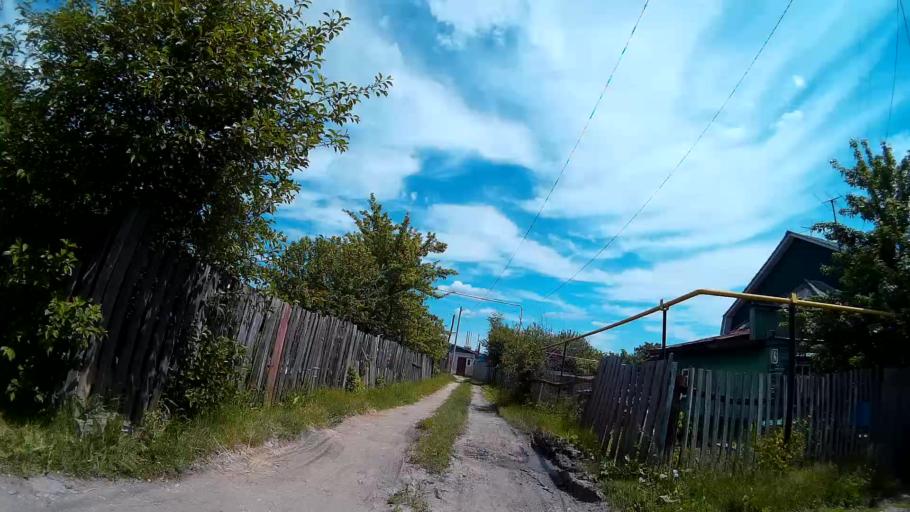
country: RU
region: Ulyanovsk
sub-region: Ulyanovskiy Rayon
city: Ulyanovsk
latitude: 54.2764
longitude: 48.3453
